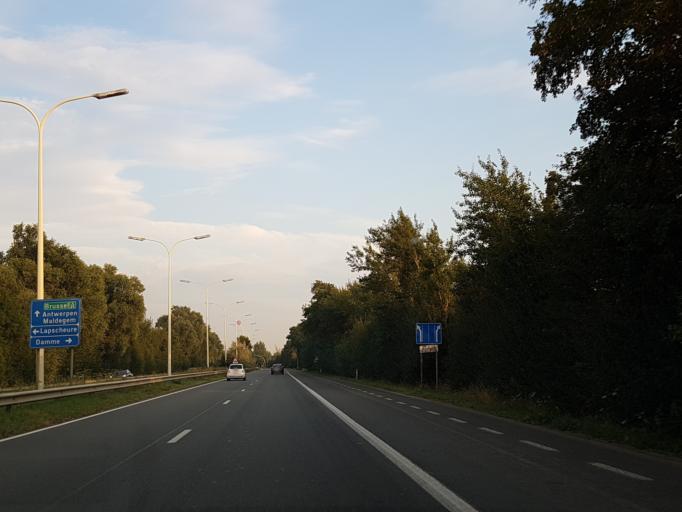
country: NL
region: Zeeland
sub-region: Gemeente Sluis
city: Sluis
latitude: 51.2793
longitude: 3.3505
